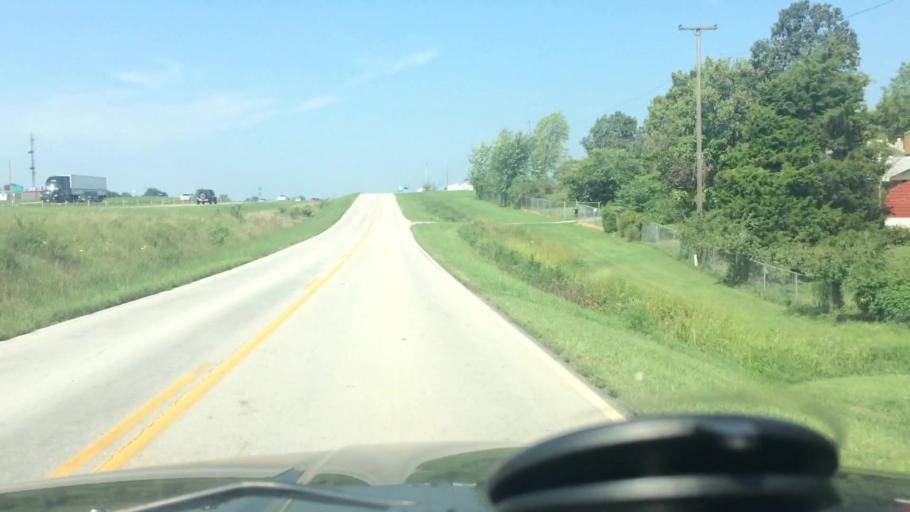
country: US
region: Missouri
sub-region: Greene County
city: Strafford
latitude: 37.2708
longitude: -93.0788
